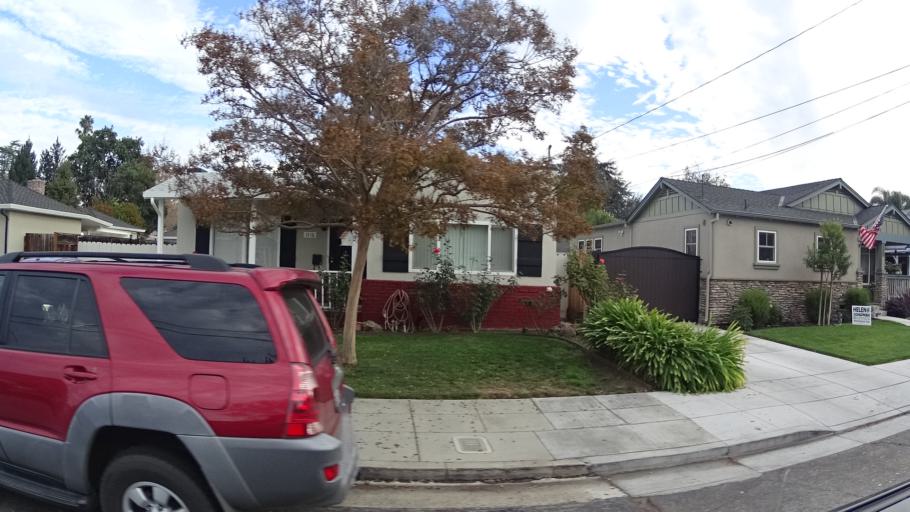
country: US
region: California
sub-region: Santa Clara County
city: Buena Vista
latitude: 37.3284
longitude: -121.9209
